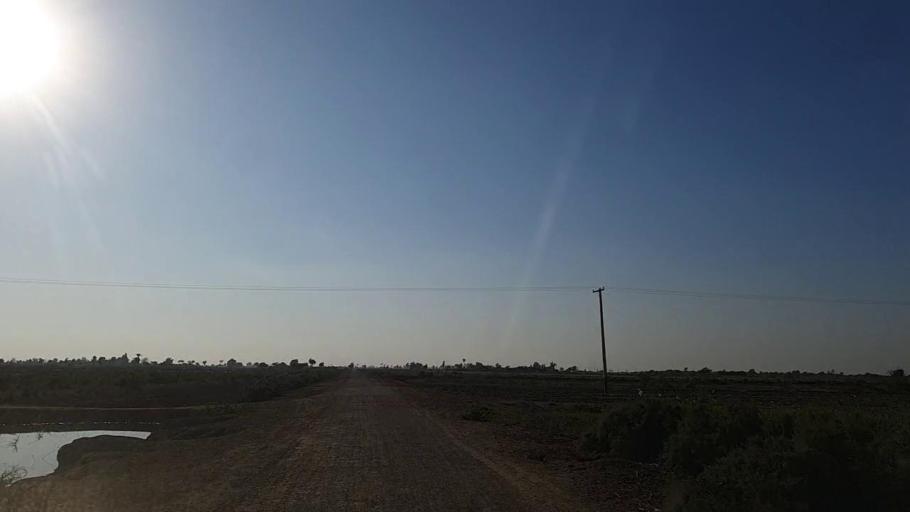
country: PK
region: Sindh
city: Samaro
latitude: 25.3442
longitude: 69.3758
